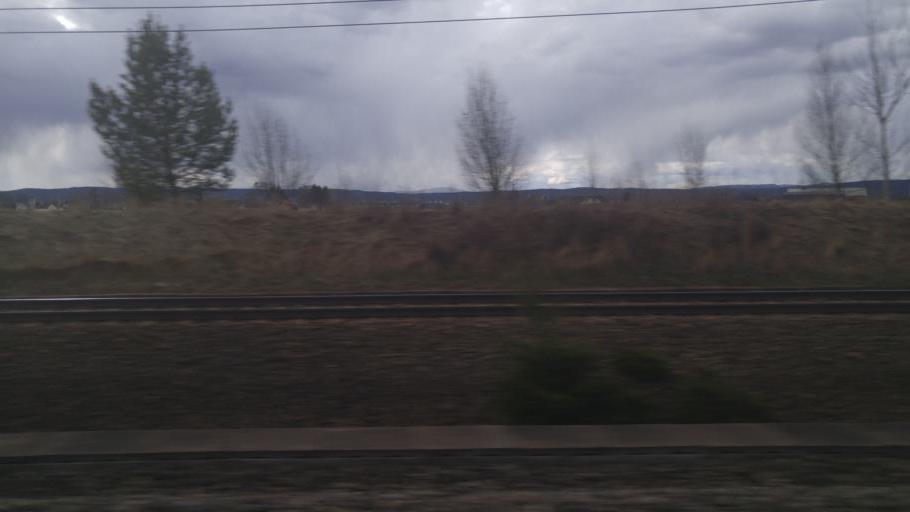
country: NO
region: Akershus
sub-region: Ullensaker
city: Klofta
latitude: 60.0896
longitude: 11.1404
